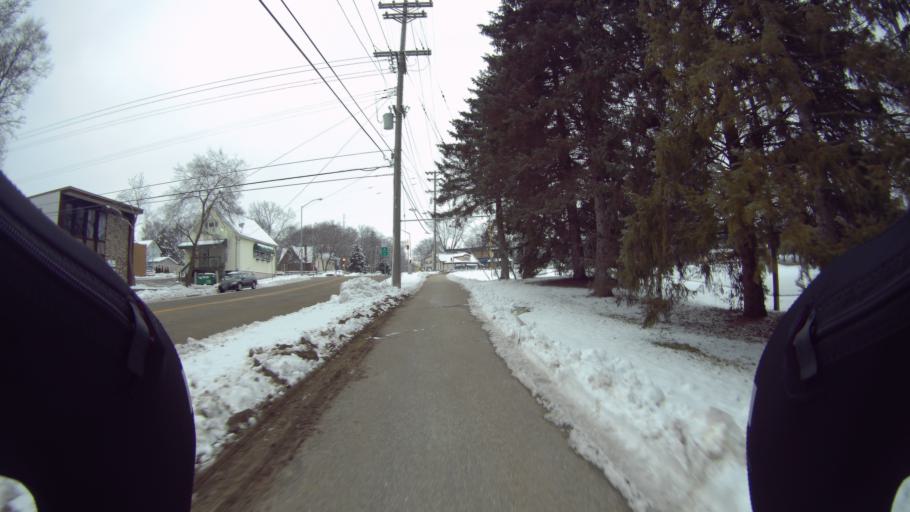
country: US
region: Wisconsin
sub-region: Dane County
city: Shorewood Hills
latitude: 43.0601
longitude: -89.4387
